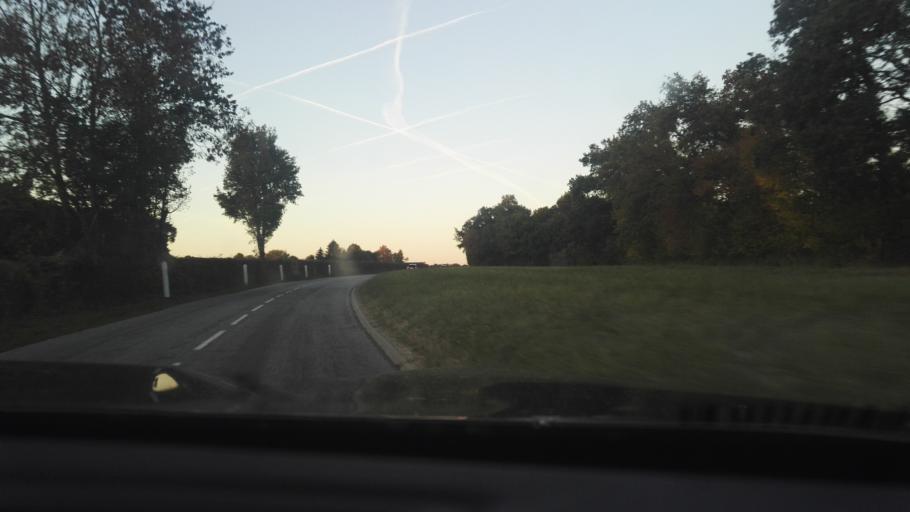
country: FR
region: Ile-de-France
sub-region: Departement des Yvelines
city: Longnes
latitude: 48.8971
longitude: 1.5828
